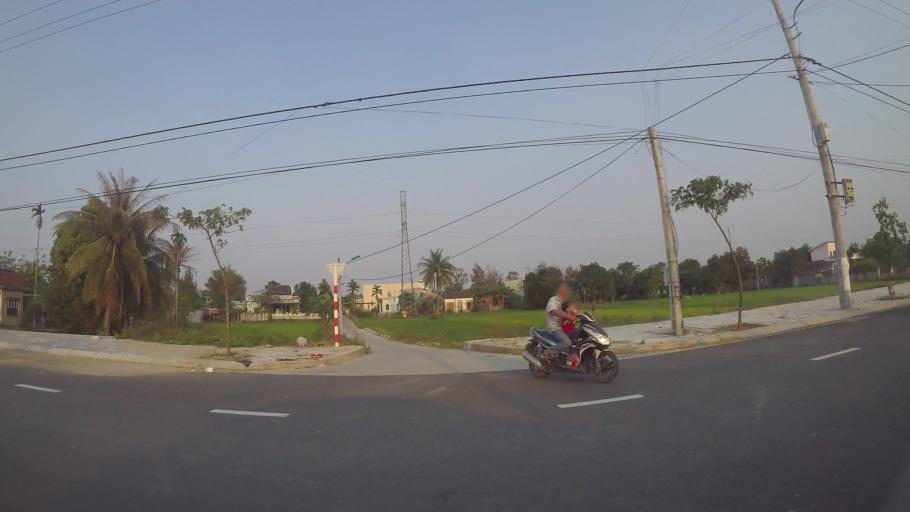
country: VN
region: Da Nang
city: Ngu Hanh Son
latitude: 15.9662
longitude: 108.2315
